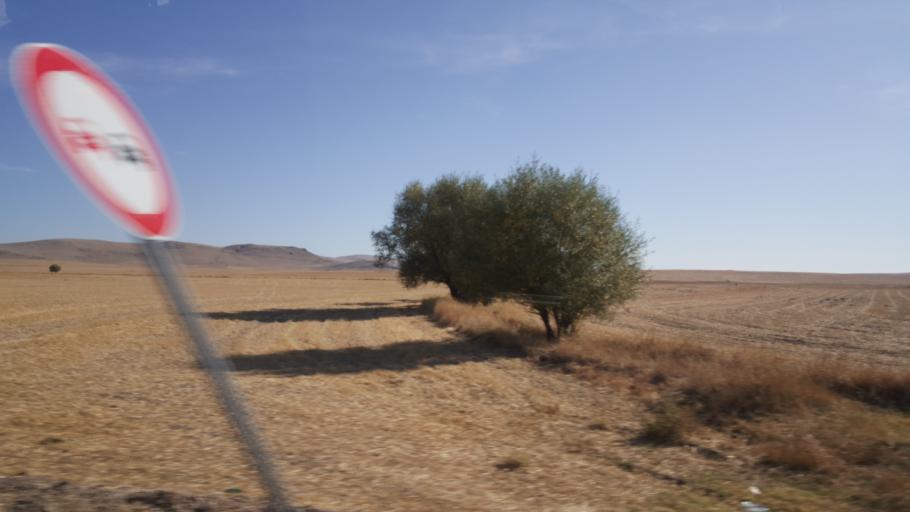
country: TR
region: Ankara
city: Yenice
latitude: 39.3485
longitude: 32.7670
